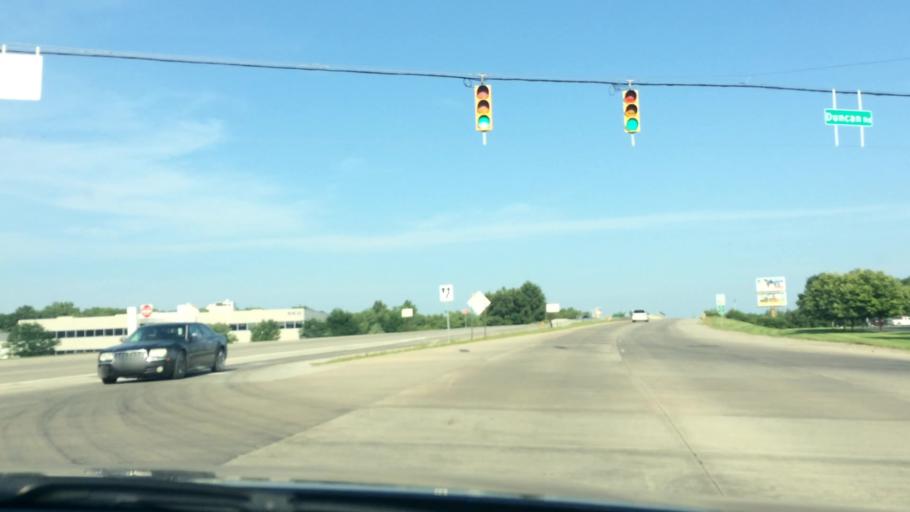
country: US
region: Indiana
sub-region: Tippecanoe County
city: Lafayette
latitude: 40.4497
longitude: -86.8804
